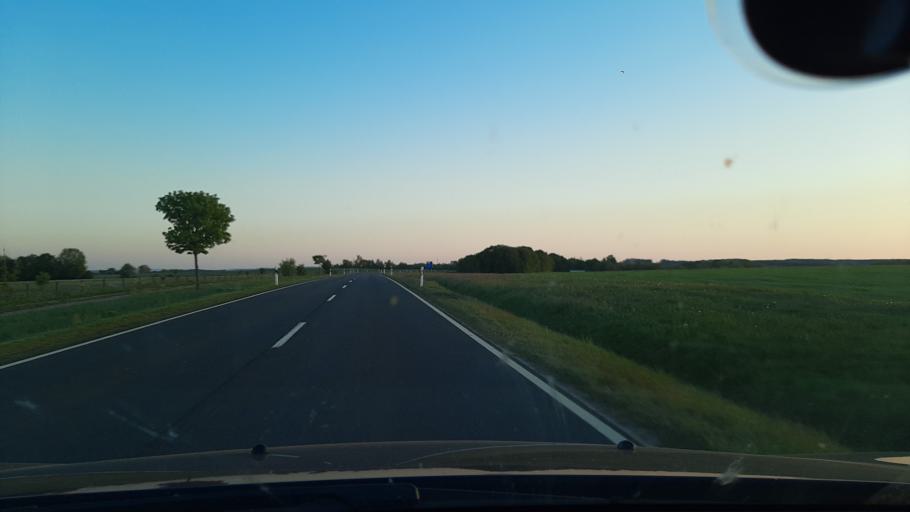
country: DE
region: Rheinland-Pfalz
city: Ohlenhard
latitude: 50.4683
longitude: 6.7048
